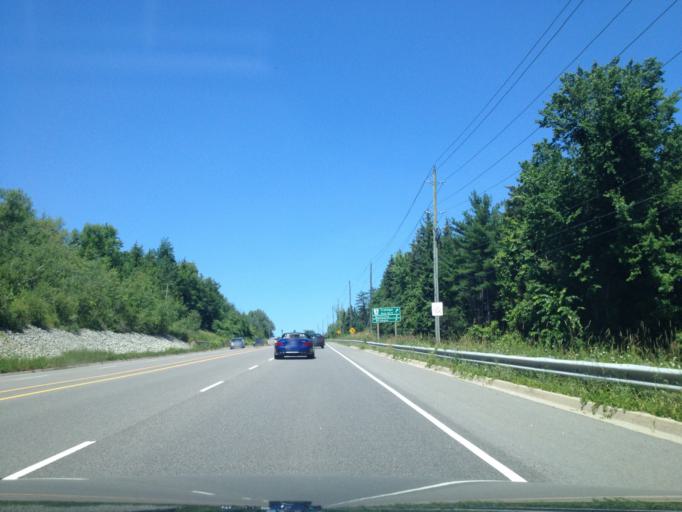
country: CA
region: Ontario
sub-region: Halton
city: Milton
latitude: 43.6689
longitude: -79.9758
